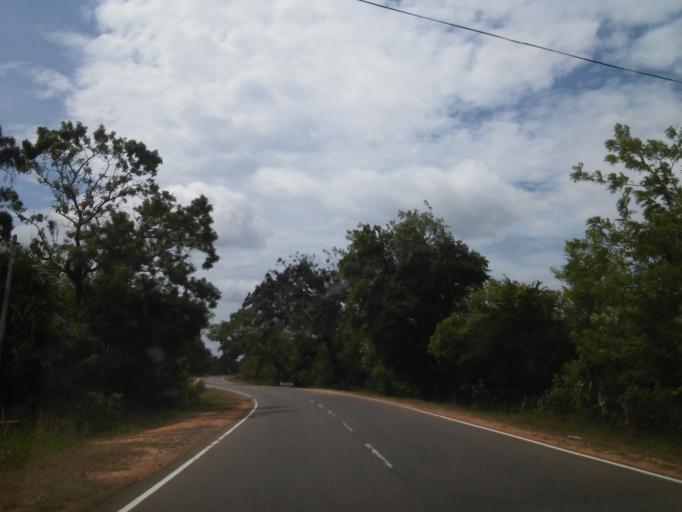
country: LK
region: Central
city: Sigiriya
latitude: 8.0792
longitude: 80.6750
